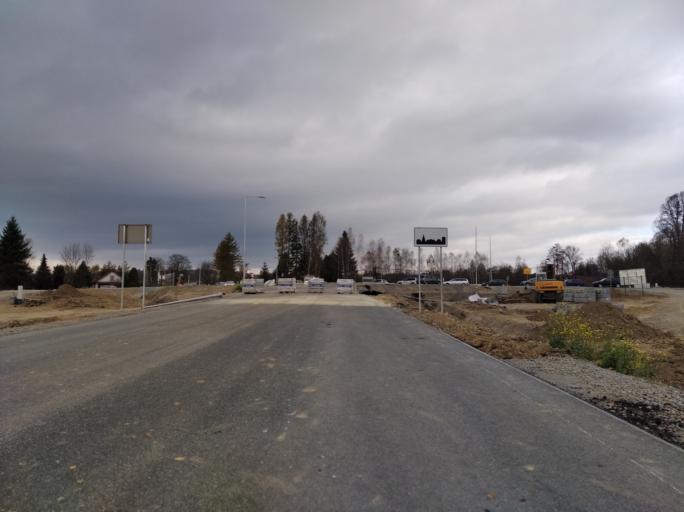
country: PL
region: Subcarpathian Voivodeship
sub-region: Powiat strzyzowski
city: Strzyzow
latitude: 49.8737
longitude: 21.7639
